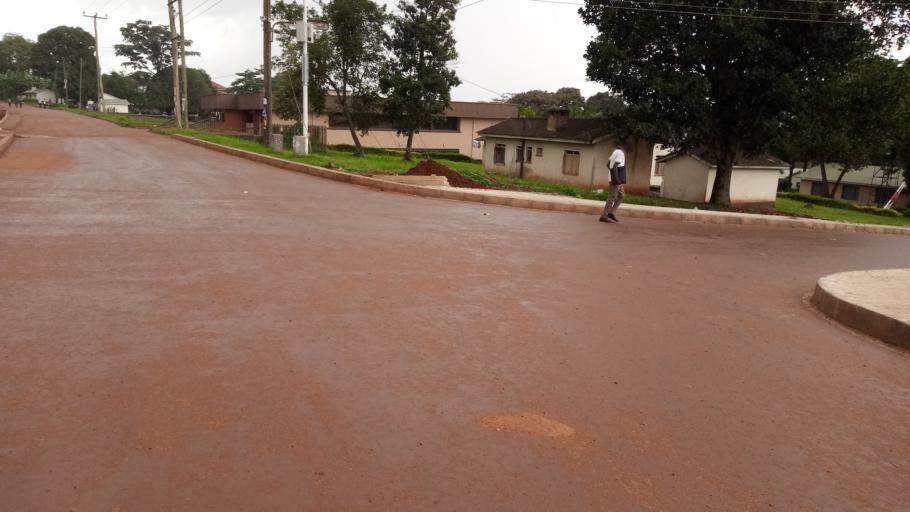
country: UG
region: Central Region
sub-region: Wakiso District
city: Kireka
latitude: 0.3491
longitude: 32.6298
